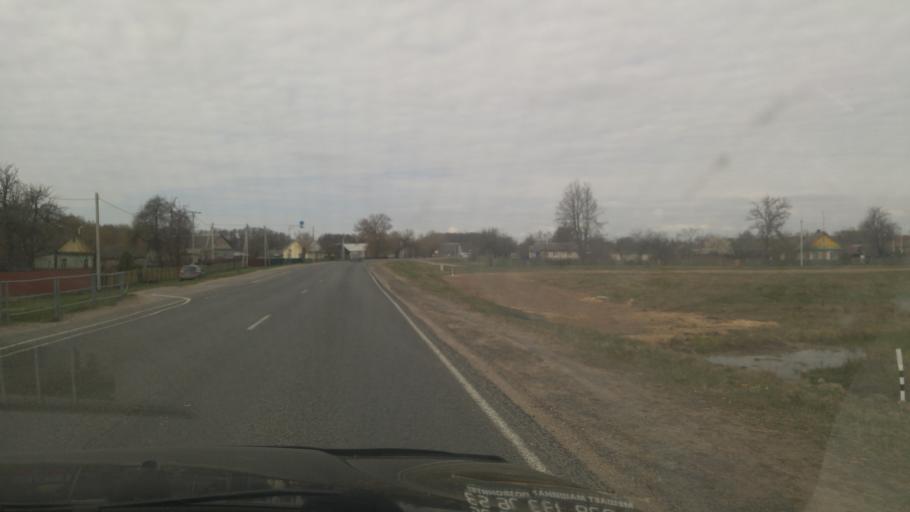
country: BY
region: Minsk
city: Blon'
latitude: 53.5241
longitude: 28.1596
